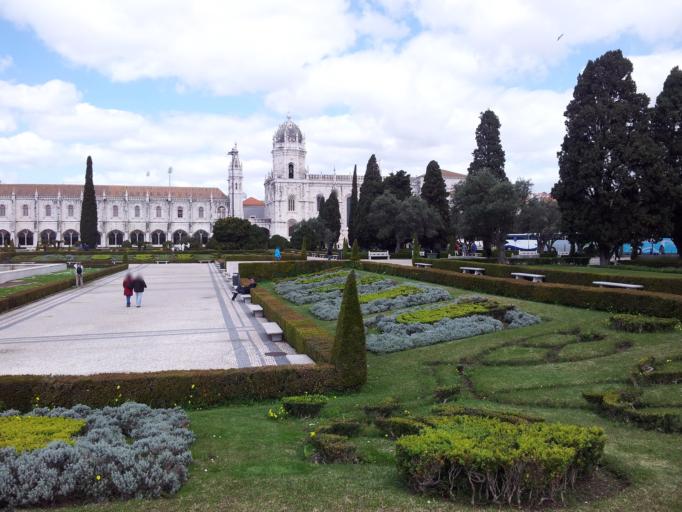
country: PT
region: Lisbon
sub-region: Oeiras
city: Alges
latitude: 38.6959
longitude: -9.2053
